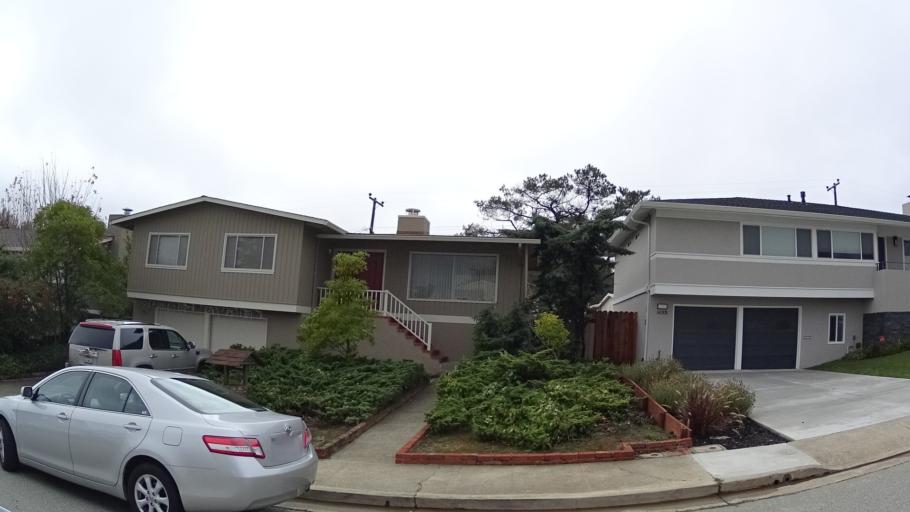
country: US
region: California
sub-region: San Mateo County
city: San Bruno
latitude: 37.6041
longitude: -122.4186
